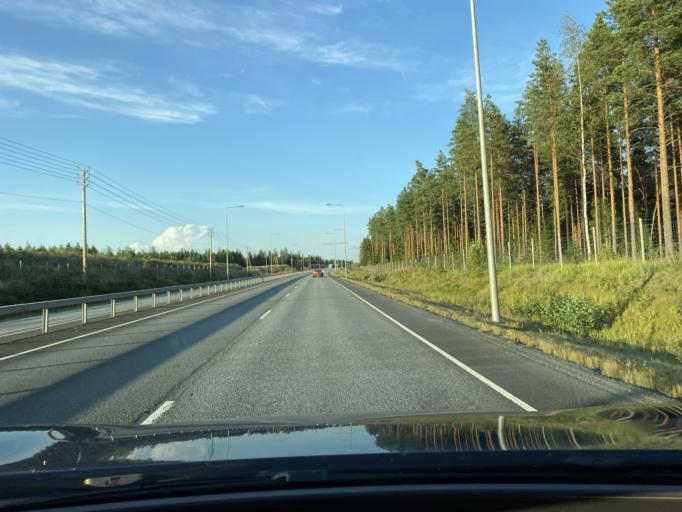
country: FI
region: Southern Ostrobothnia
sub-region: Seinaejoki
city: Seinaejoki
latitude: 62.7308
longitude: 22.8922
